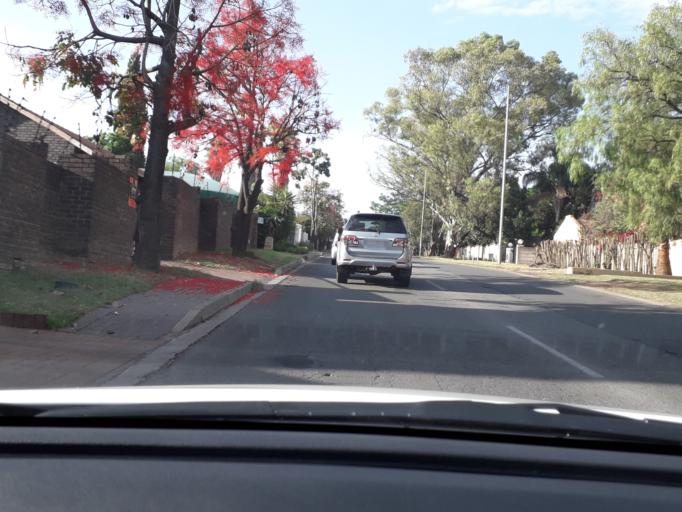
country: ZA
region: Gauteng
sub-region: City of Johannesburg Metropolitan Municipality
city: Roodepoort
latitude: -26.0757
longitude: 27.9455
